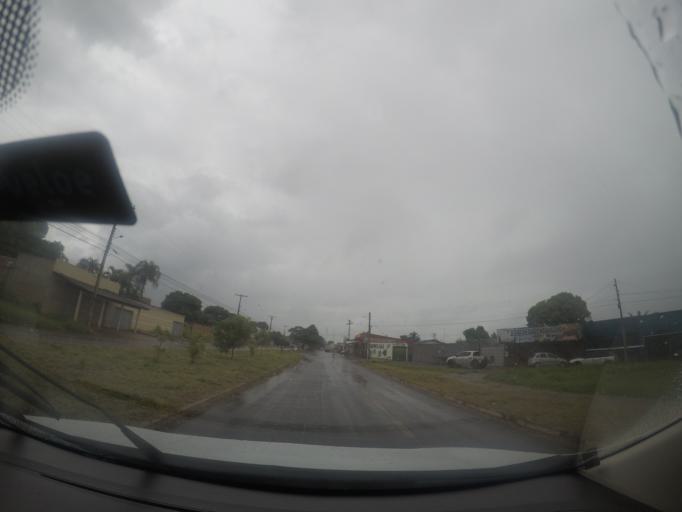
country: BR
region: Goias
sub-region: Trindade
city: Trindade
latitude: -16.6409
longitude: -49.4402
